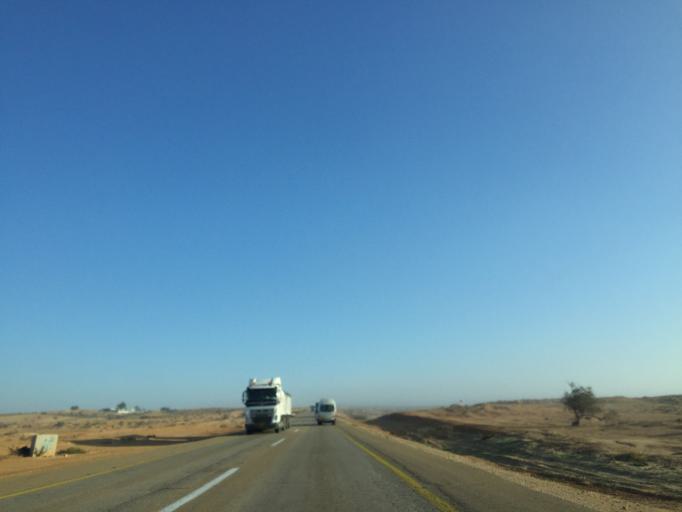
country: IL
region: Southern District
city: Yeroham
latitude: 31.0162
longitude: 34.9613
